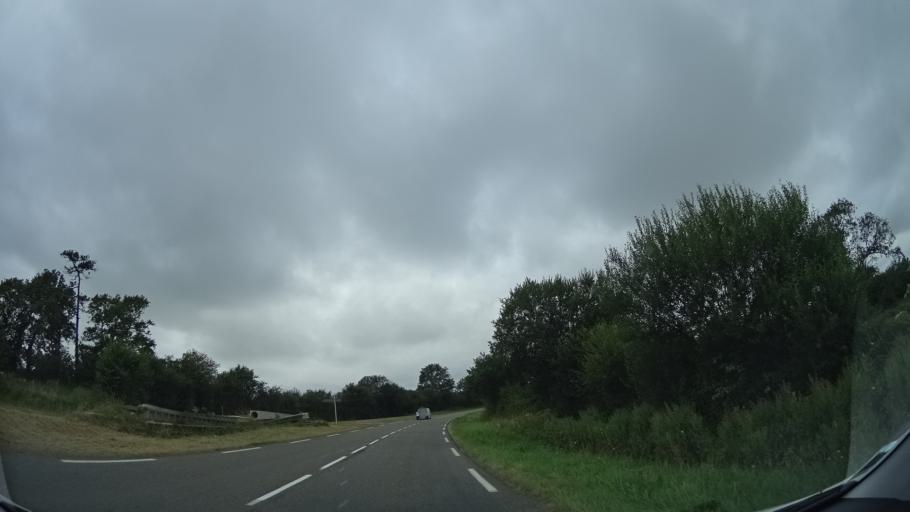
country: FR
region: Lower Normandy
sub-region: Departement de la Manche
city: Portbail
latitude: 49.3220
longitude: -1.6347
